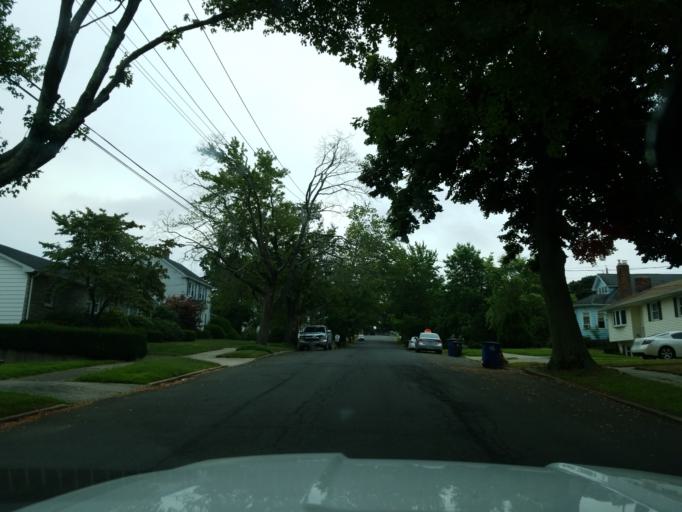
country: US
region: Connecticut
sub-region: New Haven County
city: East Haven
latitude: 41.2745
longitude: -72.8993
